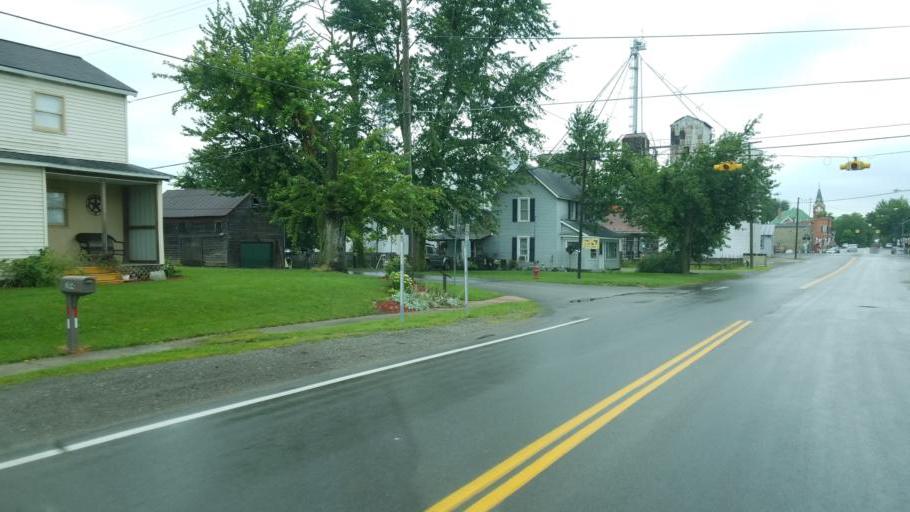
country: US
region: Ohio
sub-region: Hardin County
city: Kenton
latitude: 40.5323
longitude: -83.5199
